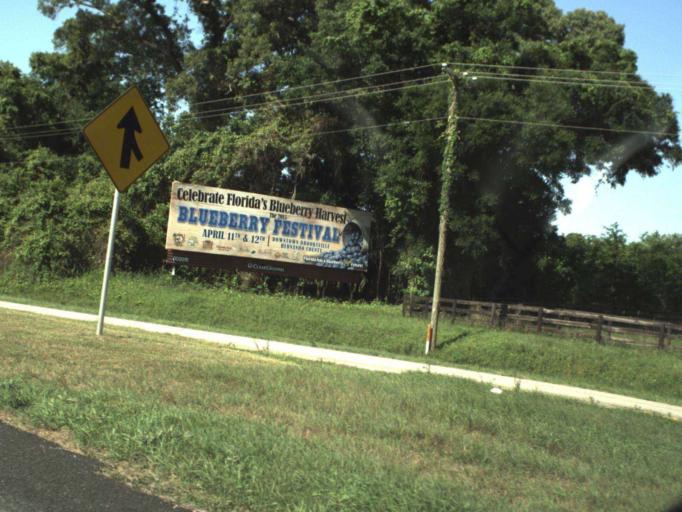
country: US
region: Florida
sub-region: Marion County
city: Citra
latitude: 29.3419
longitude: -82.1516
